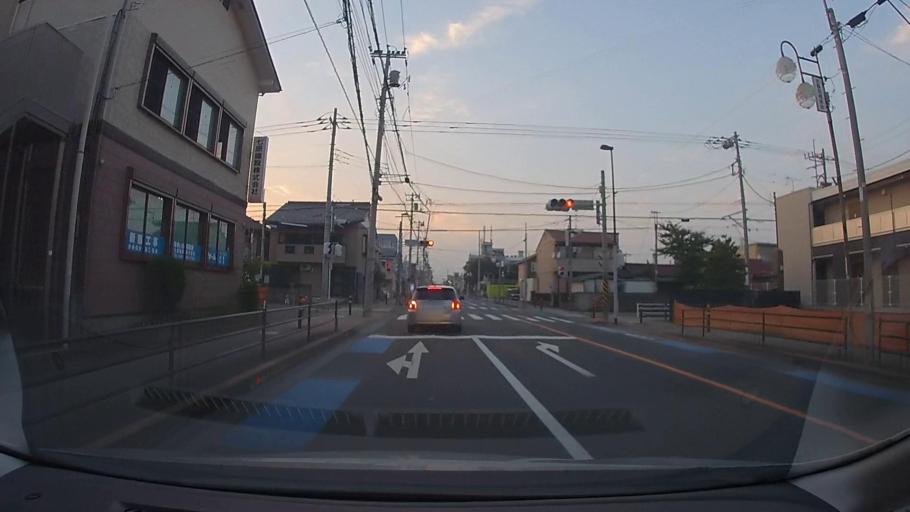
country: JP
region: Kanagawa
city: Minami-rinkan
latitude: 35.4842
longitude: 139.4504
